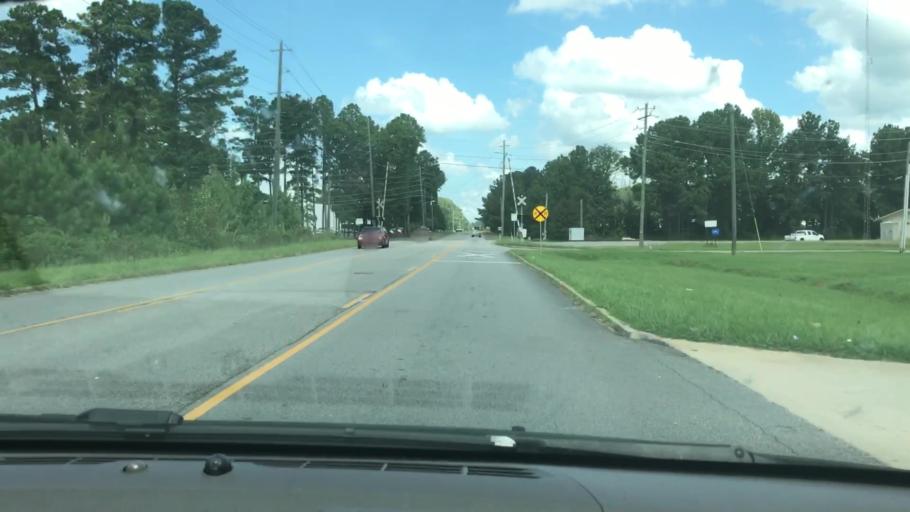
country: US
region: Georgia
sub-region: Troup County
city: La Grange
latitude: 33.0009
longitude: -85.0532
